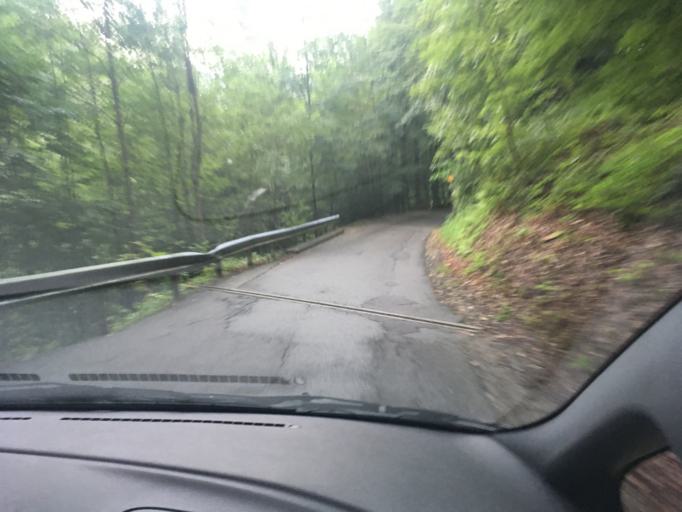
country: CH
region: Bern
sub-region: Bern-Mittelland District
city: Stettlen
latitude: 46.9443
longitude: 7.5368
